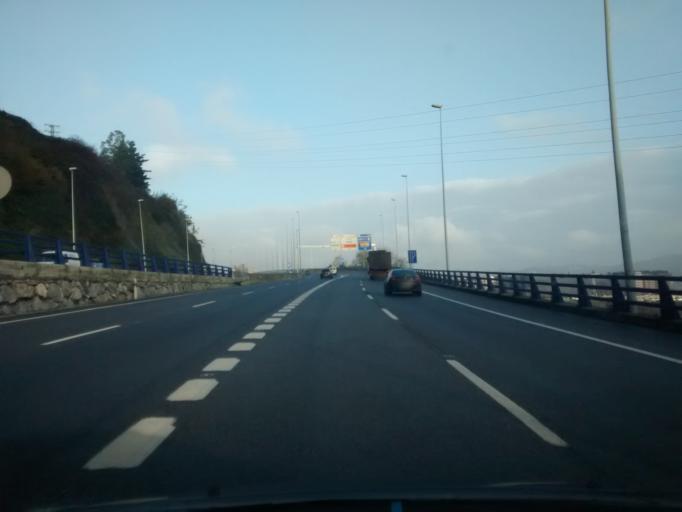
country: ES
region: Basque Country
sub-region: Bizkaia
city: Santutxu
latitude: 43.2405
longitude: -2.9268
